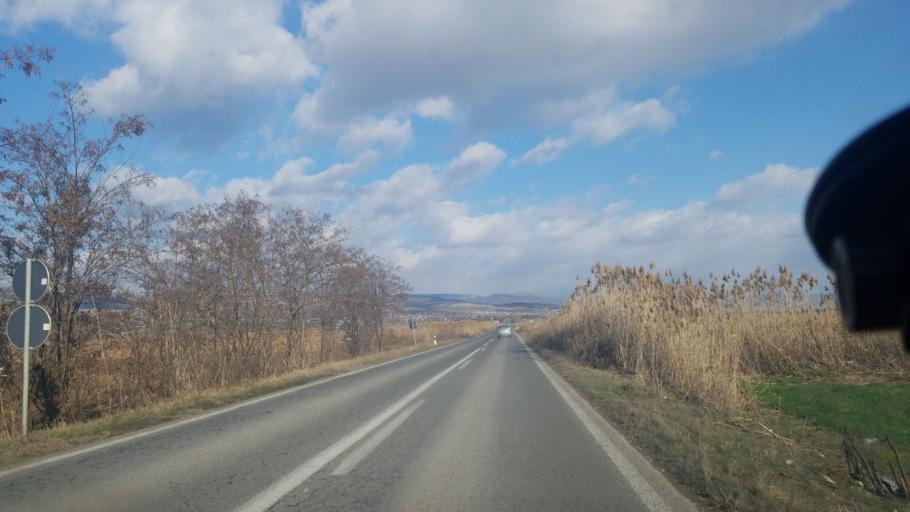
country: MK
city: Obleshevo
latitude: 41.8875
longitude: 22.3417
